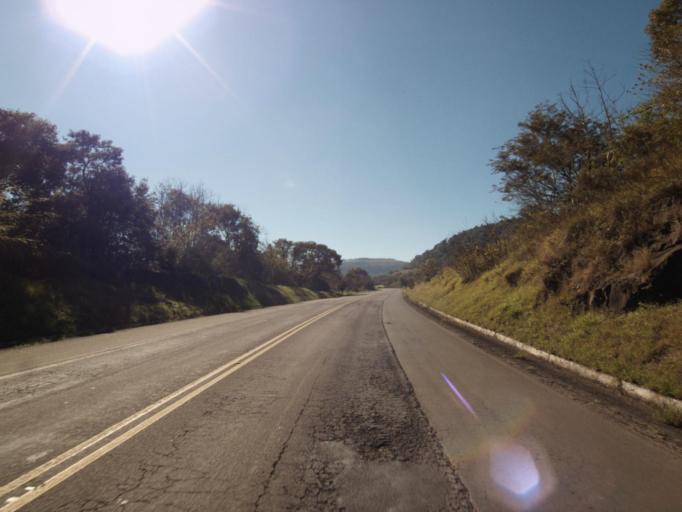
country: BR
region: Rio Grande do Sul
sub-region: Frederico Westphalen
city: Frederico Westphalen
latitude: -26.9858
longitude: -53.2256
